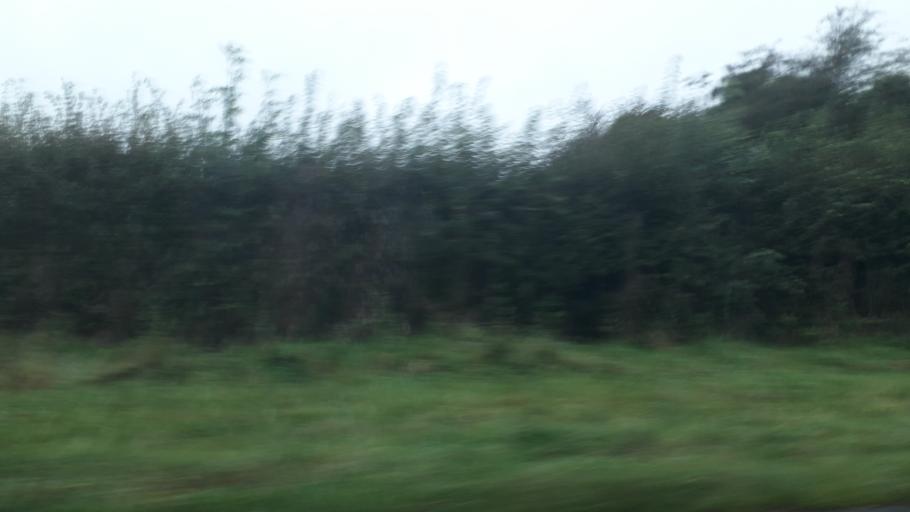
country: IE
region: Leinster
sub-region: An Longfort
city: Edgeworthstown
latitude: 53.6627
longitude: -7.5284
